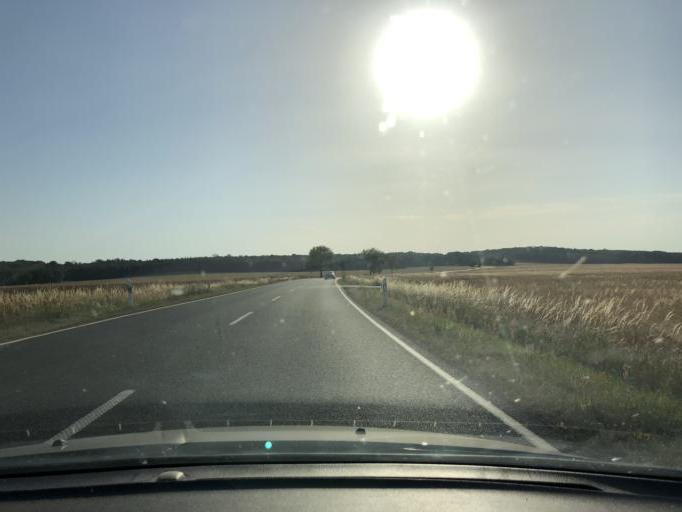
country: DE
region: Saxony
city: Wermsdorf
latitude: 51.3307
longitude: 12.9429
